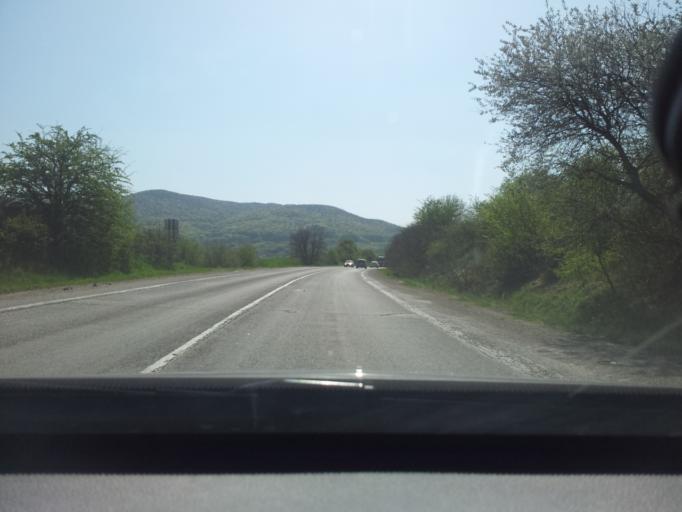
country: SK
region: Trenciansky
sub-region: Okres Trencin
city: Trencin
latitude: 48.8430
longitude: 18.0526
